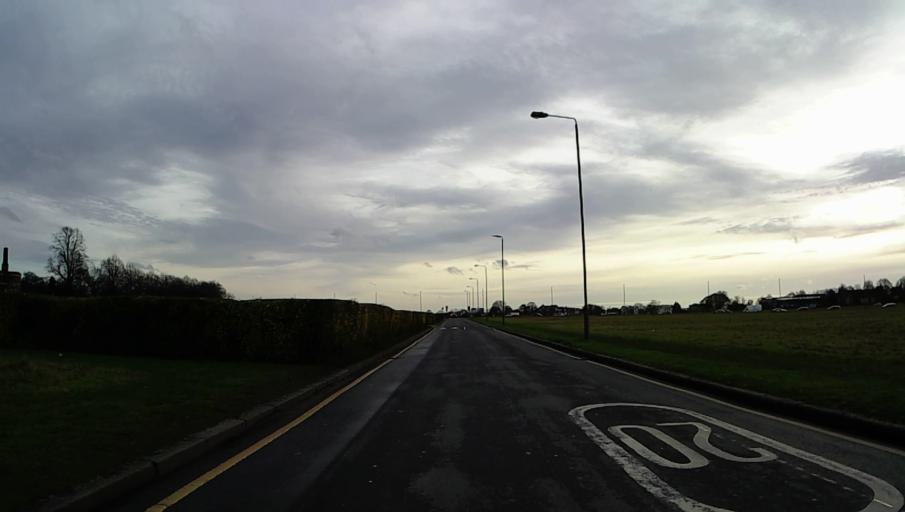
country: GB
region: England
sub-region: Greater London
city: Blackheath
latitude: 51.4738
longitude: -0.0034
